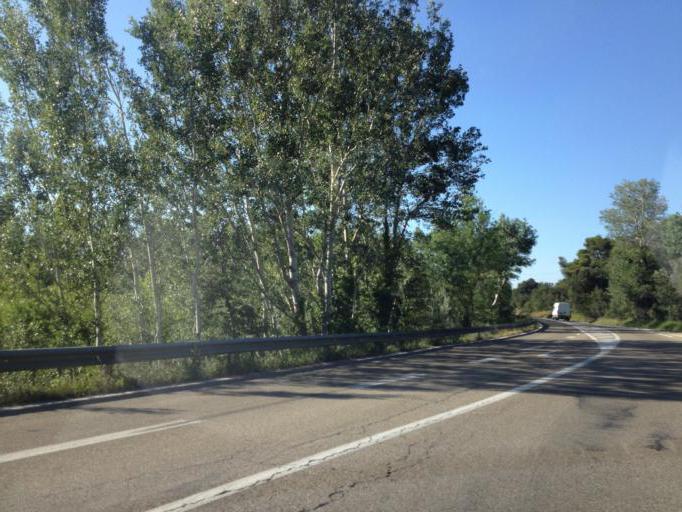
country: FR
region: Languedoc-Roussillon
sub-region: Departement du Gard
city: Montfaucon
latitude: 44.0806
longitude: 4.7774
